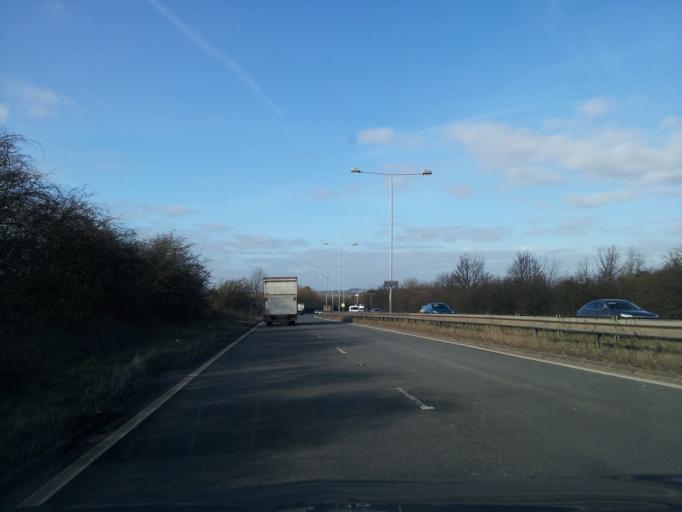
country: GB
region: England
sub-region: Nottinghamshire
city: Ruddington
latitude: 52.9117
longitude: -1.1560
